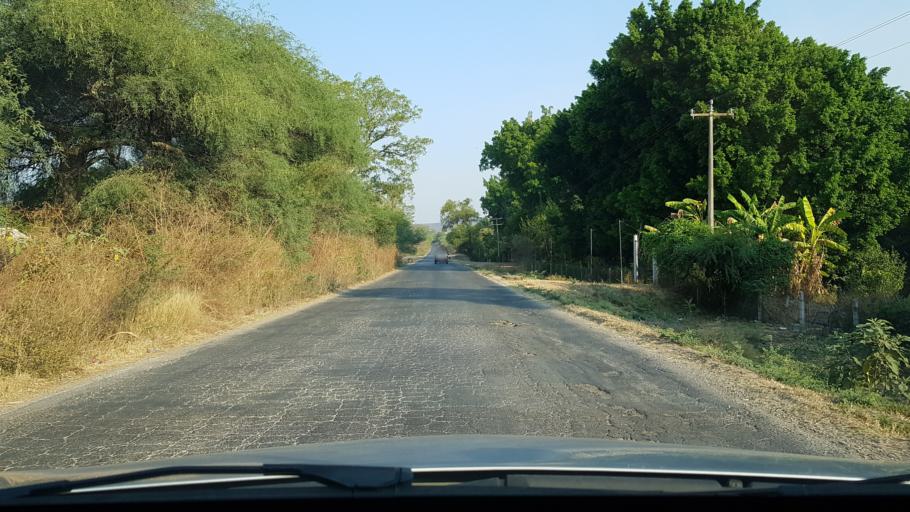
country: MX
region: Morelos
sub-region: Tepalcingo
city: Zacapalco
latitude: 18.6444
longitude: -99.0219
